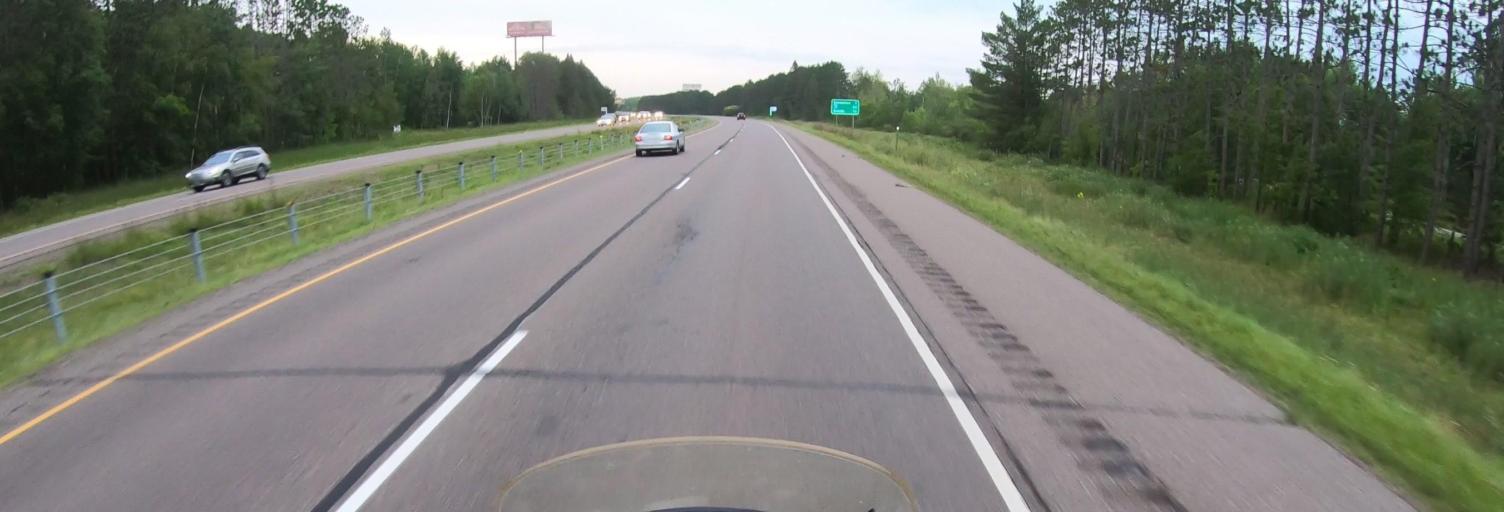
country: US
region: Minnesota
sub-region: Pine County
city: Hinckley
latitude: 46.0224
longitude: -92.9262
